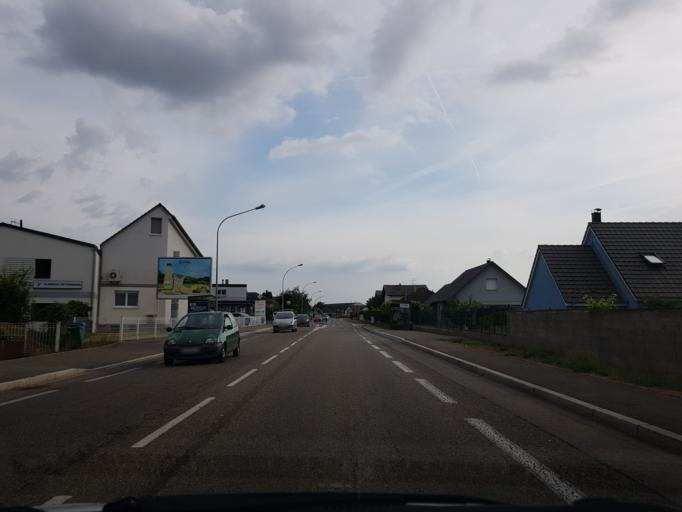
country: FR
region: Alsace
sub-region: Departement du Haut-Rhin
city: Wittenheim
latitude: 47.8147
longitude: 7.3382
